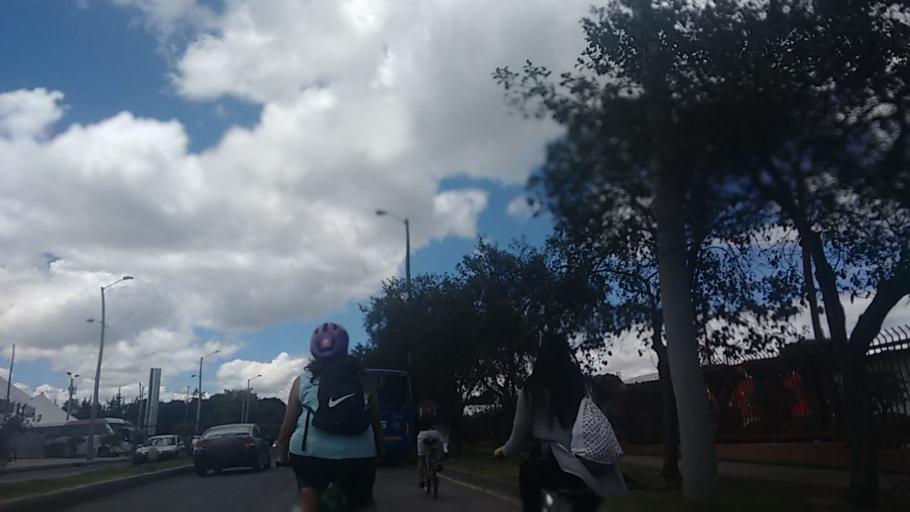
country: CO
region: Cundinamarca
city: Cota
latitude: 4.7707
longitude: -74.0412
